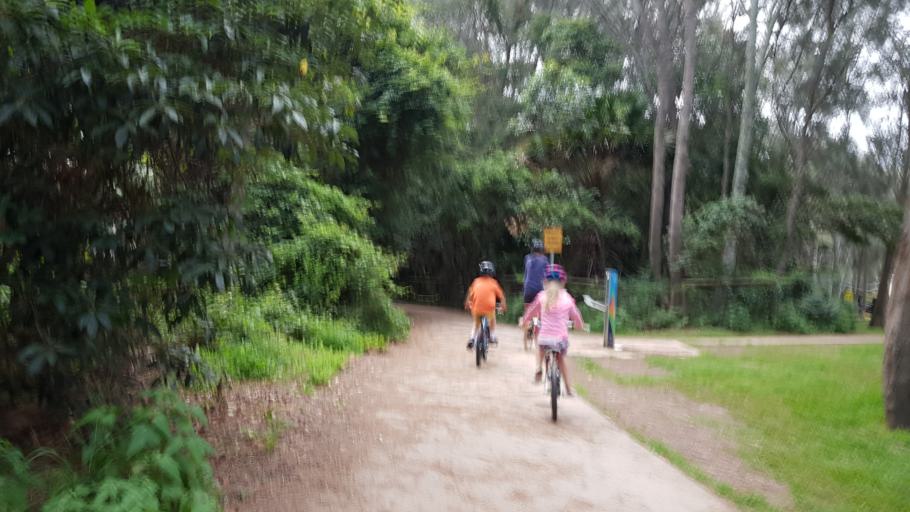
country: AU
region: New South Wales
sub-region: Warringah
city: Narrabeen
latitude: -33.7191
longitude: 151.2883
